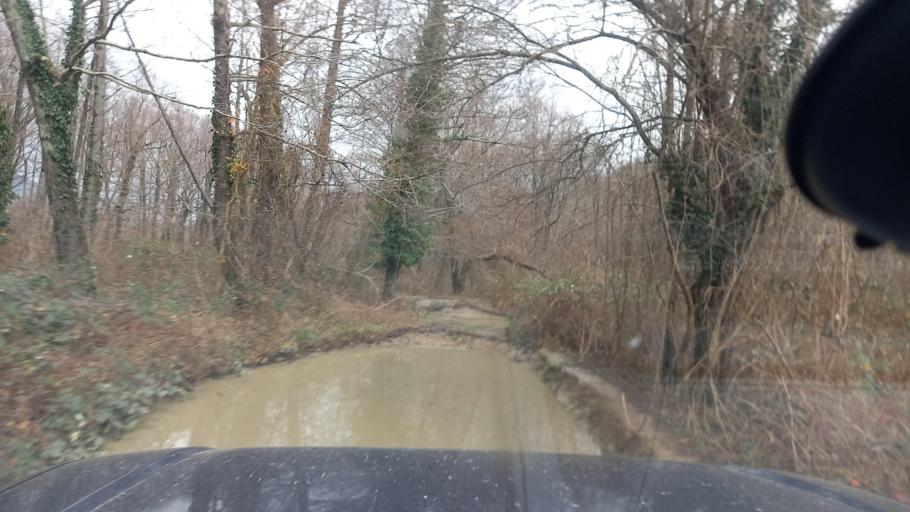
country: RU
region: Krasnodarskiy
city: Pshada
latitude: 44.4848
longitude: 38.4097
